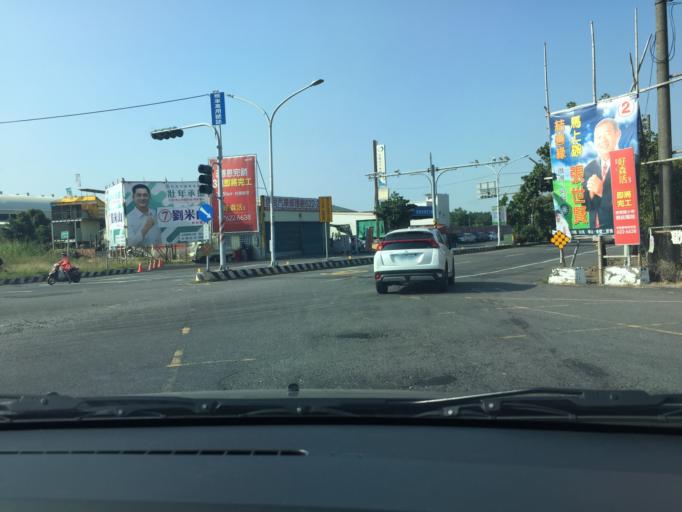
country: TW
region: Taiwan
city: Xinying
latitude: 23.2692
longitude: 120.3136
